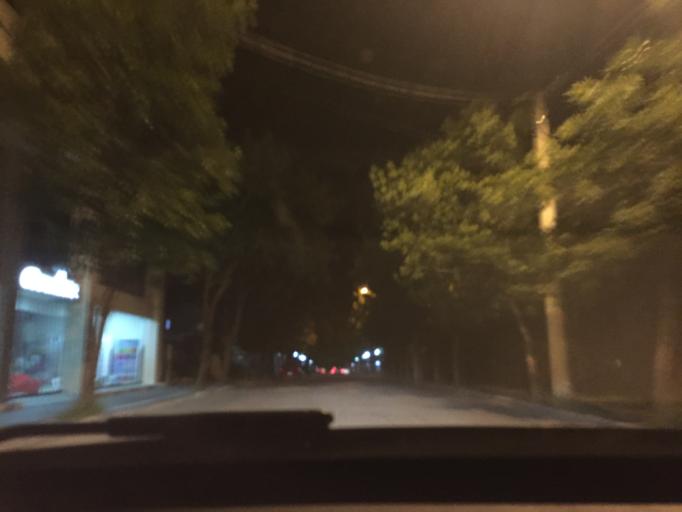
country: AR
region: Cordoba
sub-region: Departamento de Calamuchita
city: Santa Rosa de Calamuchita
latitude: -32.0656
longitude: -64.5401
